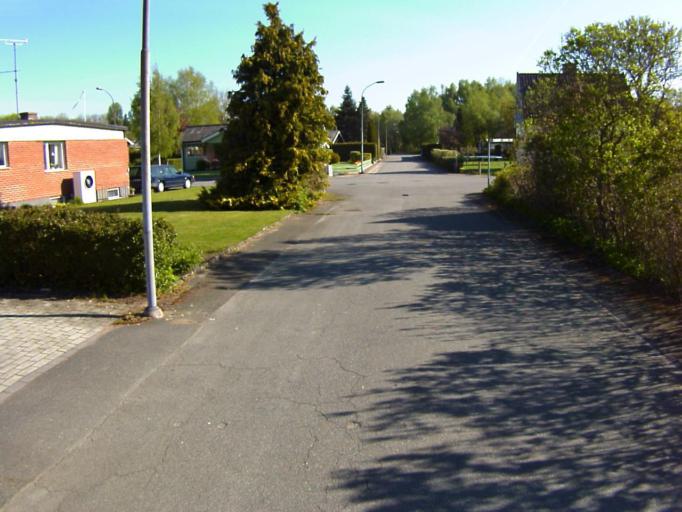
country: SE
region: Skane
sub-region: Kristianstads Kommun
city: Onnestad
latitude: 55.9328
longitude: 13.9641
